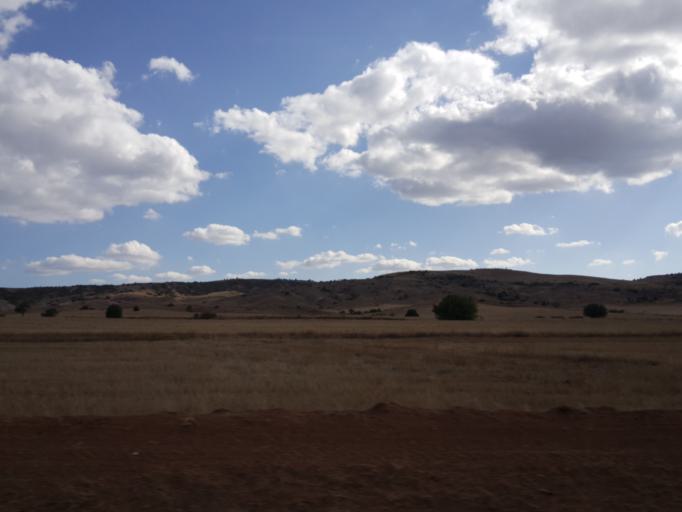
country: TR
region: Tokat
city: Sulusaray
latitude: 39.9866
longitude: 35.9637
